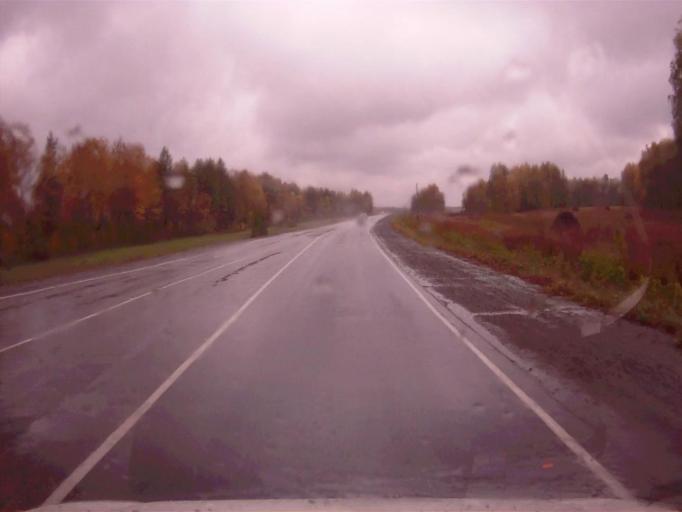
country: RU
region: Chelyabinsk
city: Roshchino
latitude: 55.4002
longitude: 61.0742
